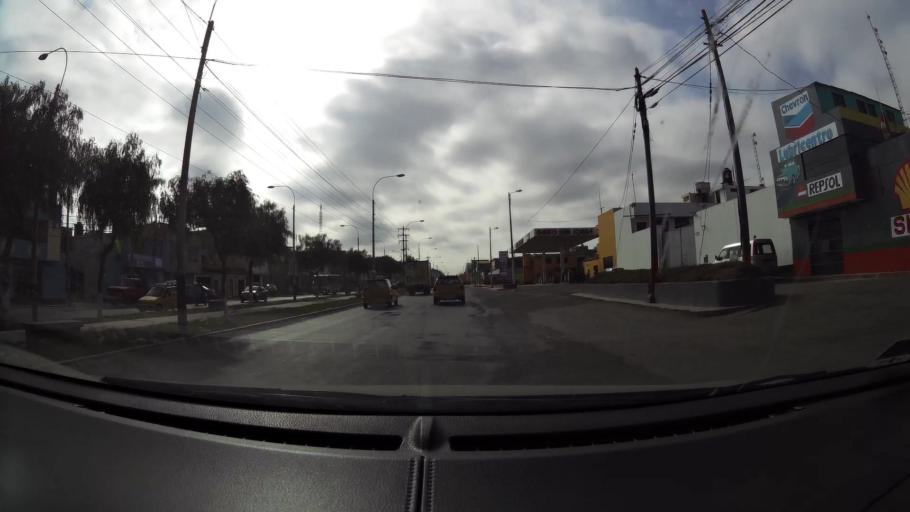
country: PE
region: La Libertad
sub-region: Provincia de Trujillo
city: La Esperanza
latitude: -8.0909
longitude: -79.0364
